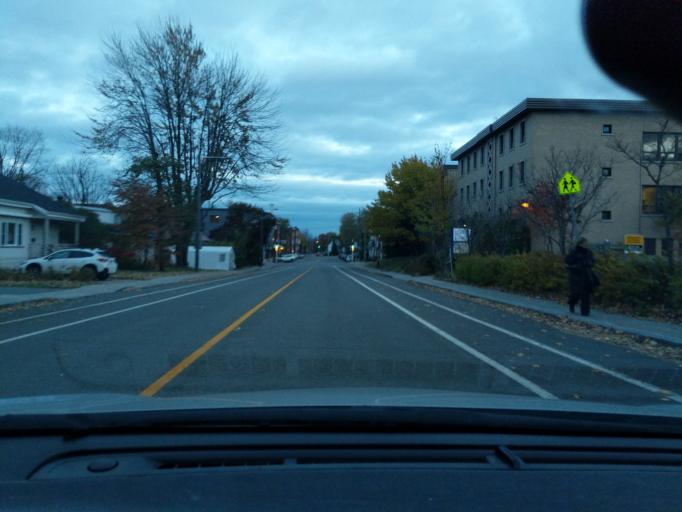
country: CA
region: Quebec
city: Quebec
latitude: 46.7853
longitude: -71.2491
